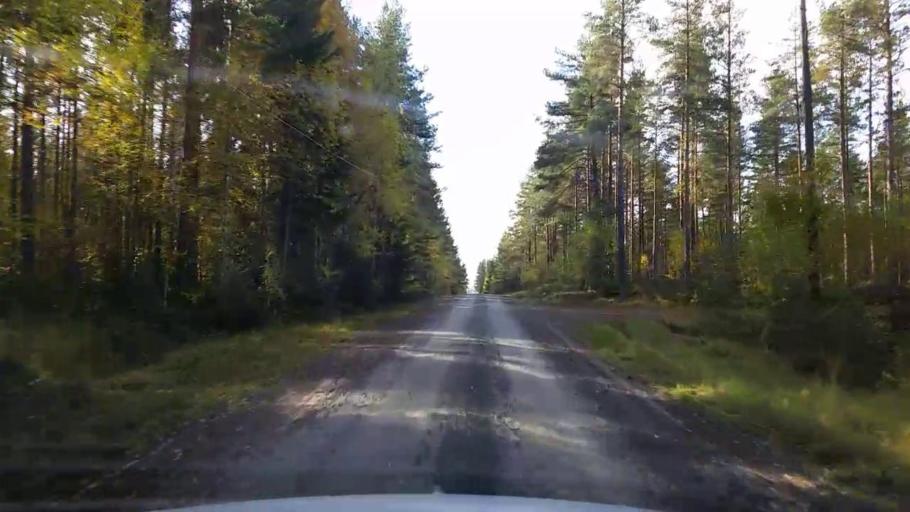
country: SE
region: Gaevleborg
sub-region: Ljusdals Kommun
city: Jaervsoe
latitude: 61.7883
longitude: 16.1701
